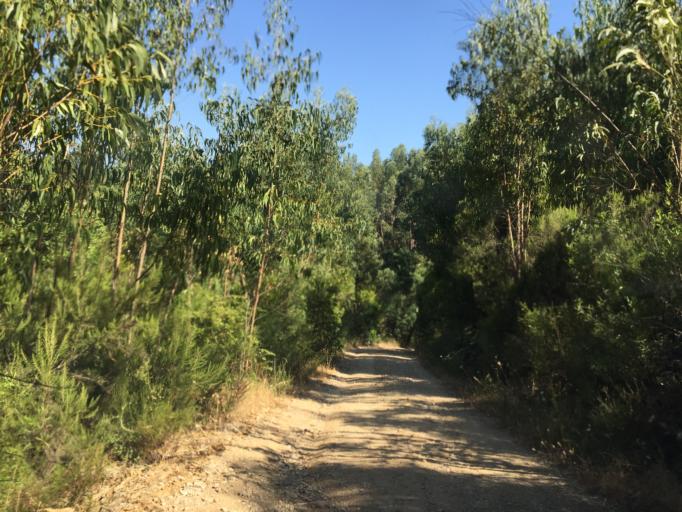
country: PT
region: Santarem
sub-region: Tomar
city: Tomar
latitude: 39.6137
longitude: -8.3522
